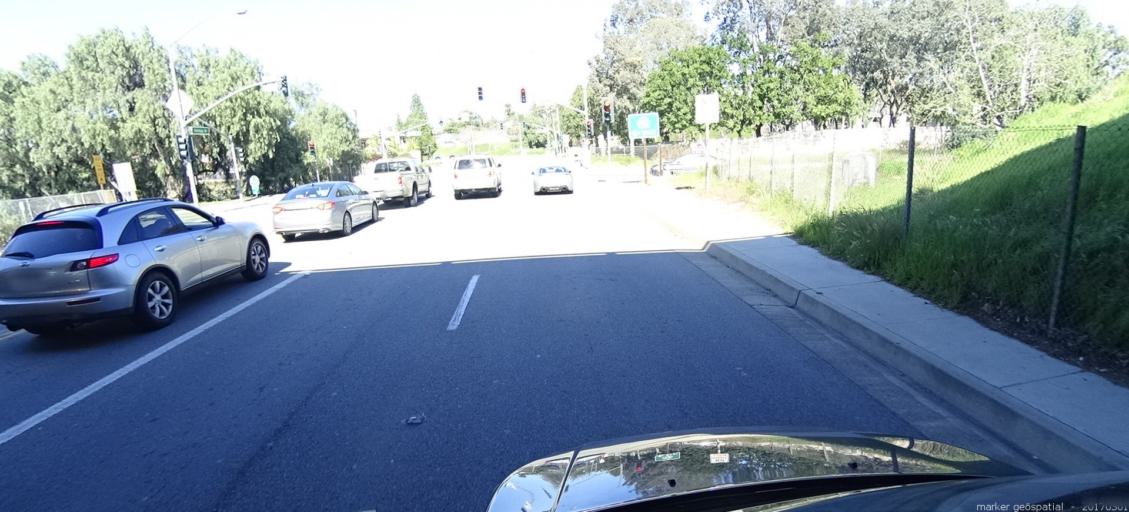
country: US
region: California
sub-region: Orange County
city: Yorba Linda
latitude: 33.8738
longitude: -117.8030
